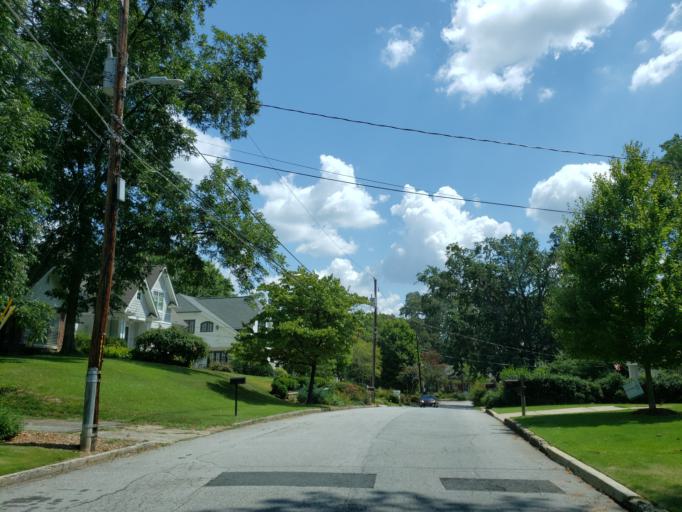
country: US
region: Georgia
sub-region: DeKalb County
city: Druid Hills
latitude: 33.7932
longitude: -84.3606
